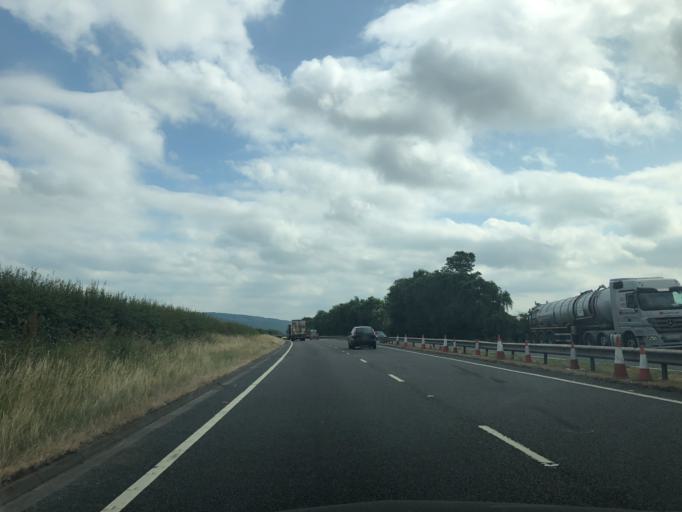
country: GB
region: England
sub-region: Stockton-on-Tees
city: Yarm
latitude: 54.4345
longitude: -1.3235
